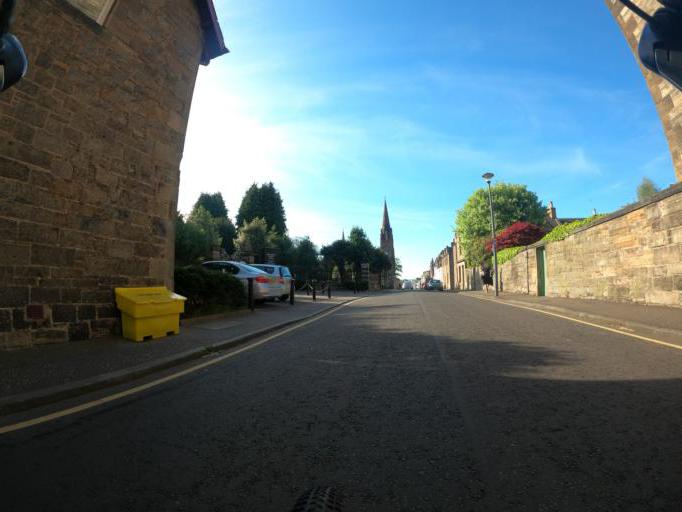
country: GB
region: Scotland
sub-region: Edinburgh
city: Edinburgh
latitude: 55.9535
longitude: -3.2204
